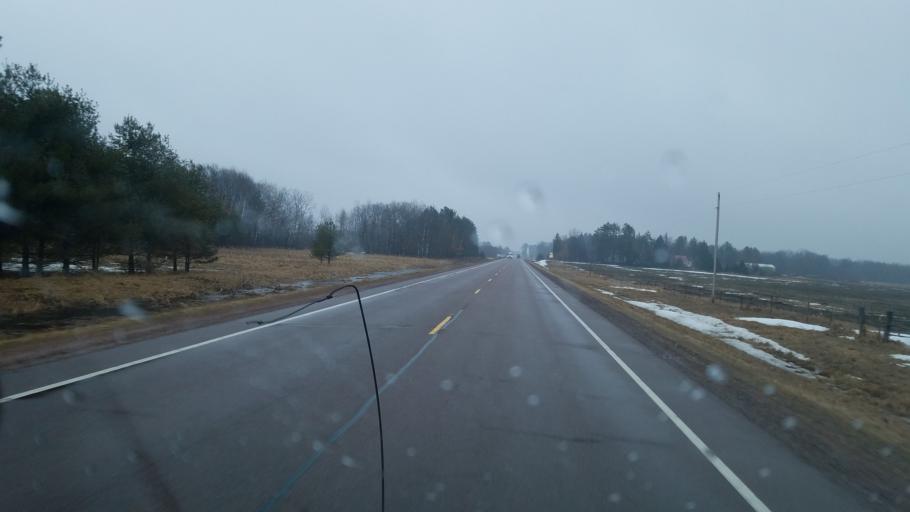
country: US
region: Wisconsin
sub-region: Wood County
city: Marshfield
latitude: 44.4535
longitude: -90.2854
